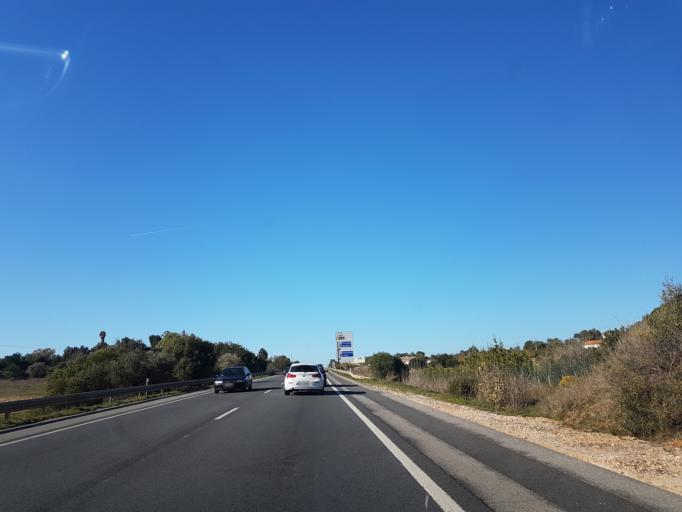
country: PT
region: Faro
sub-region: Portimao
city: Portimao
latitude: 37.1541
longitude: -8.5279
